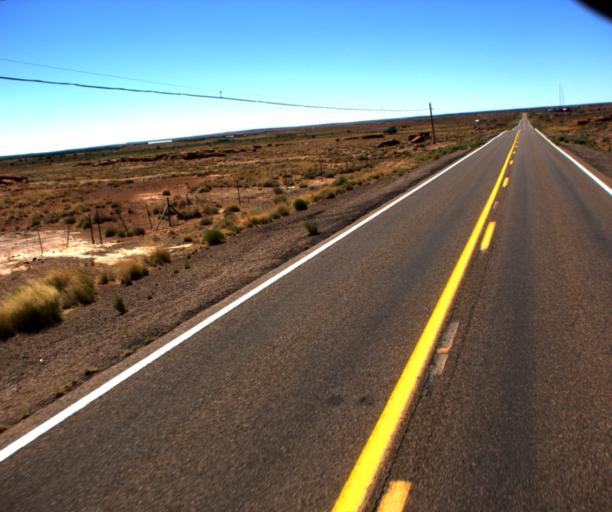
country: US
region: Arizona
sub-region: Navajo County
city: Winslow
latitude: 34.9903
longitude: -110.6671
